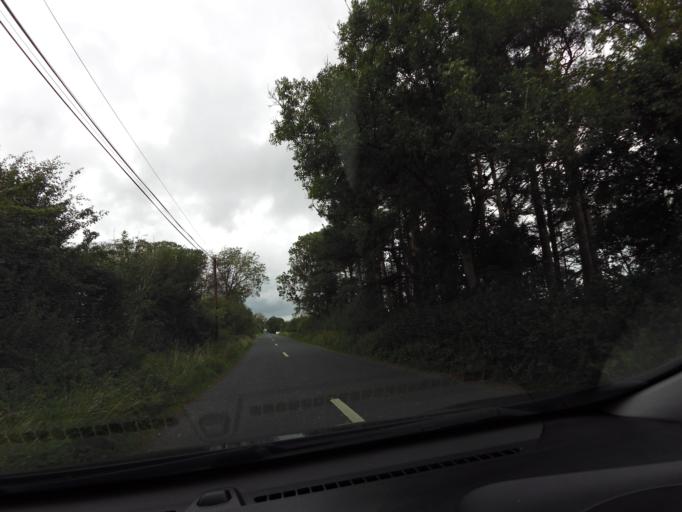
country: IE
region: Connaught
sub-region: County Galway
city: Athenry
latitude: 53.3008
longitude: -8.6259
